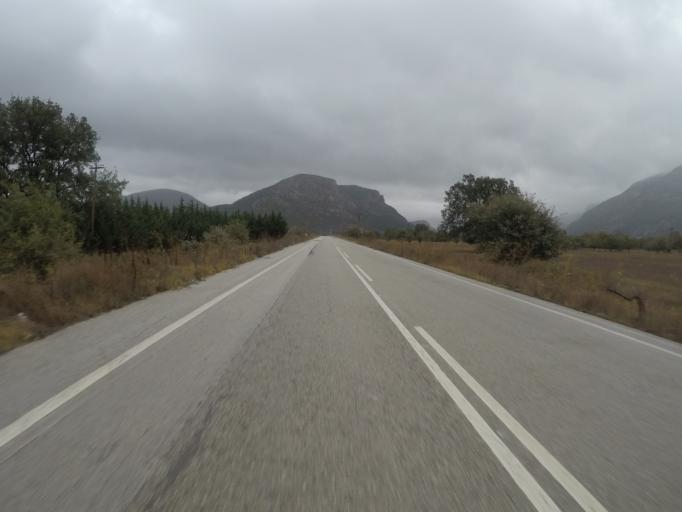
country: GR
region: Peloponnese
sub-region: Nomos Arkadias
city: Tripoli
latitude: 37.5868
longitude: 22.4258
